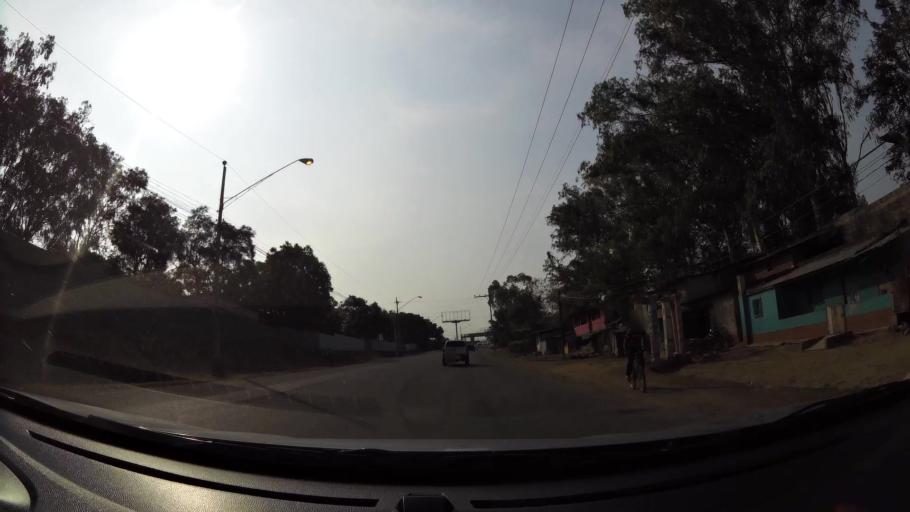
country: HN
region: Comayagua
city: Comayagua
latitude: 14.4511
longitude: -87.6455
